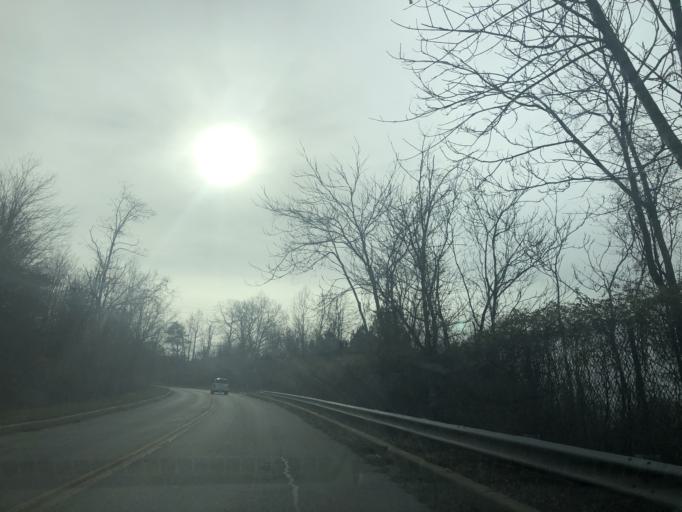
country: US
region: Maryland
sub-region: Howard County
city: Elkridge
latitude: 39.2104
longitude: -76.6941
